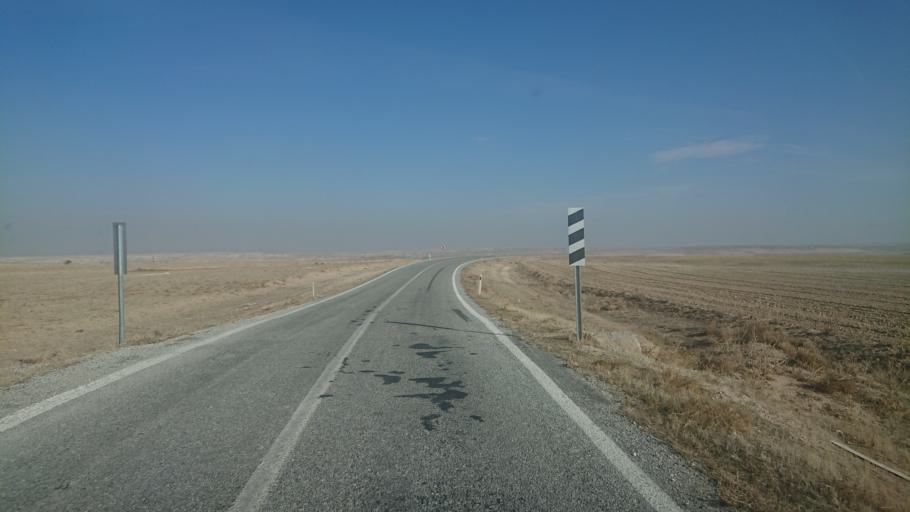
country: TR
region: Aksaray
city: Sultanhani
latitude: 38.0363
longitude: 33.5830
